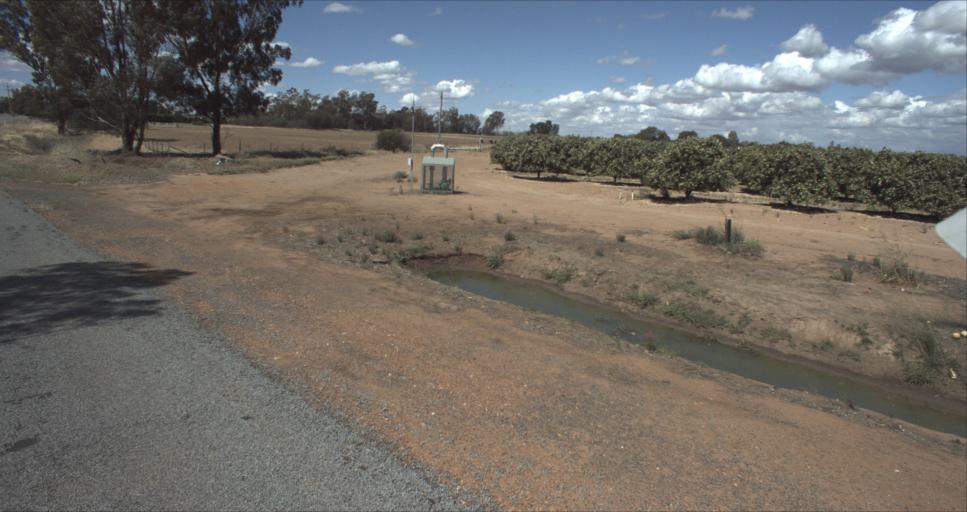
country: AU
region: New South Wales
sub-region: Leeton
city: Leeton
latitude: -34.5179
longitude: 146.2281
